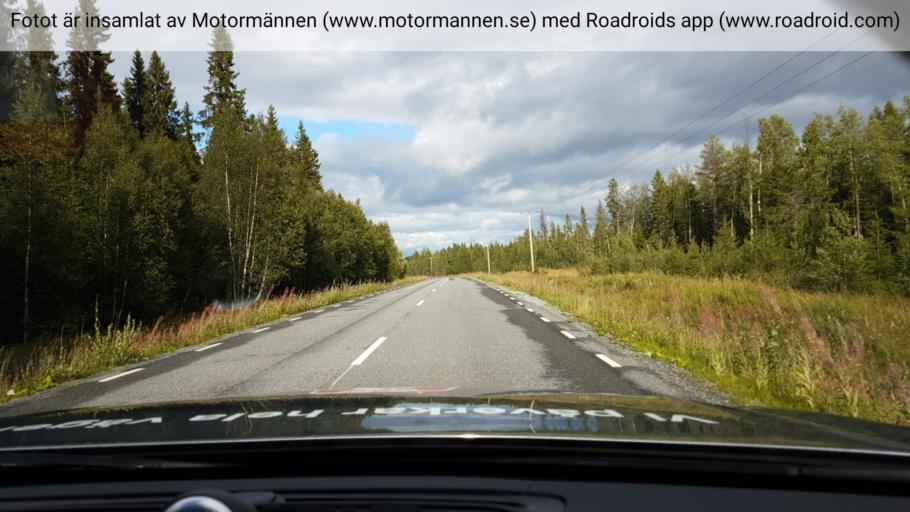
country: SE
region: Jaemtland
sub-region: Krokoms Kommun
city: Krokom
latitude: 63.6497
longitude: 14.4569
